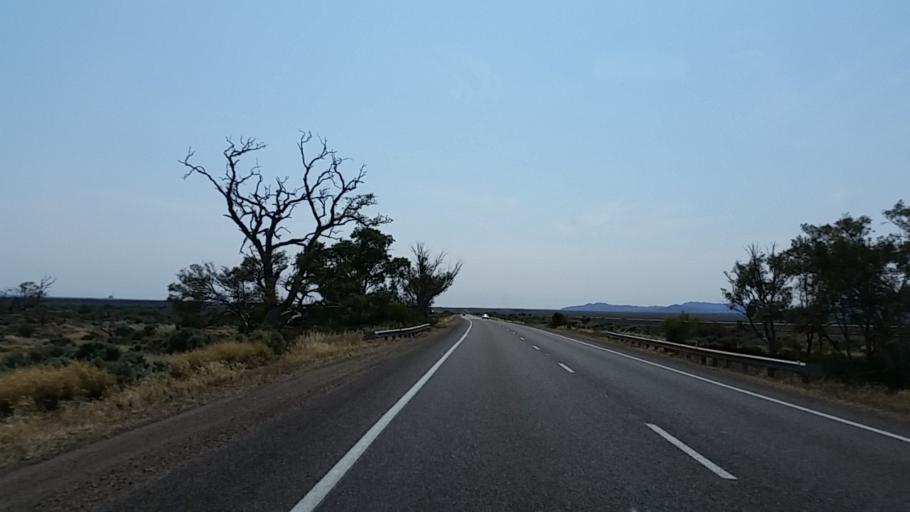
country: AU
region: South Australia
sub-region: Port Augusta
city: Port Augusta
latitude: -32.6901
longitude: 137.9408
